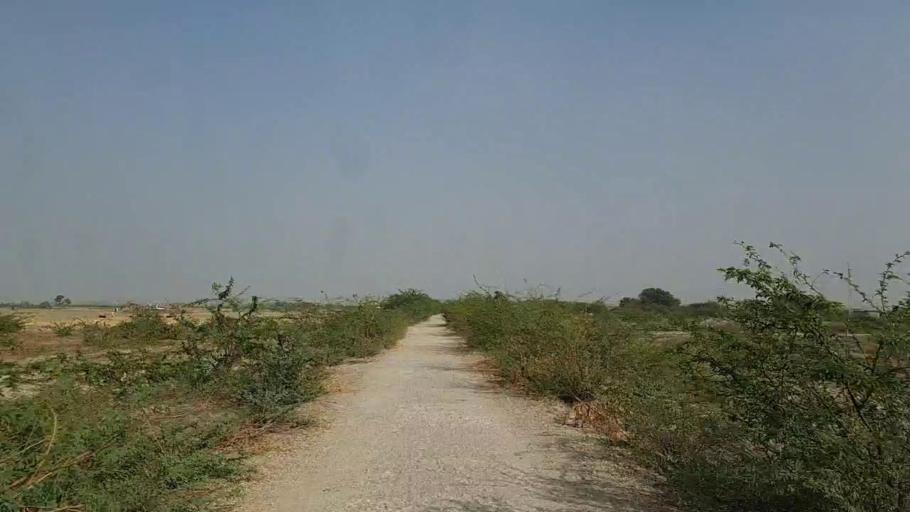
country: PK
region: Sindh
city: Naukot
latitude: 24.6676
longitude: 69.2723
